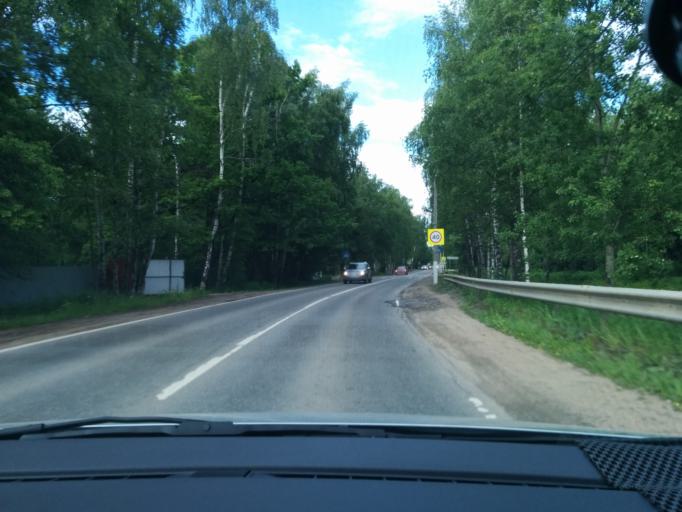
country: RU
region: Moskovskaya
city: Lugovaya
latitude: 56.0354
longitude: 37.4691
